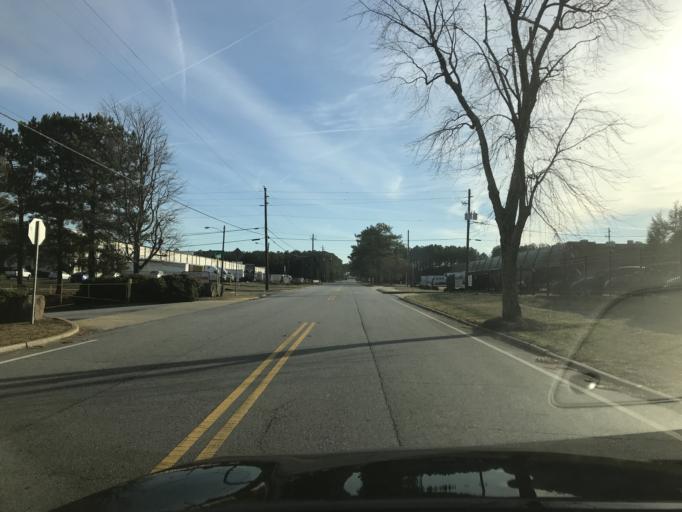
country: US
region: Georgia
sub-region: Clayton County
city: Morrow
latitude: 33.5668
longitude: -84.3537
